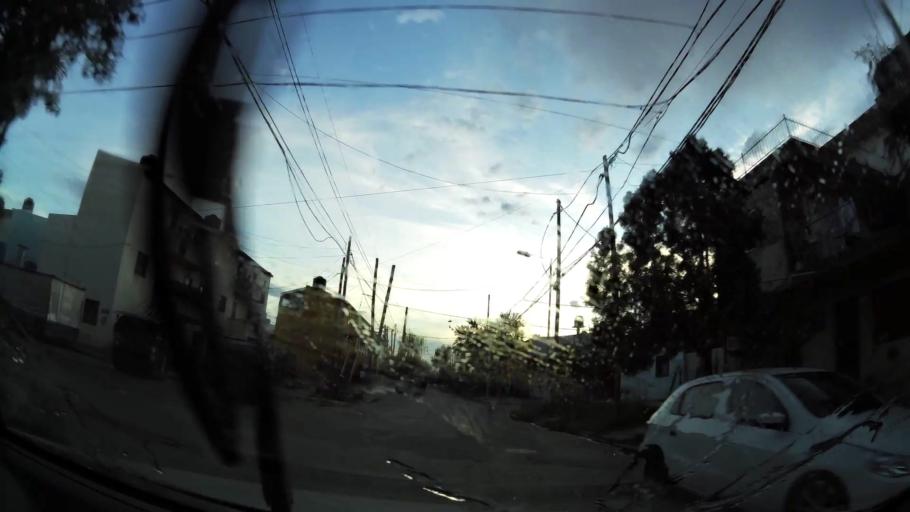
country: AR
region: Buenos Aires
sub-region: Partido de Avellaneda
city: Avellaneda
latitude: -34.6835
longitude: -58.3297
